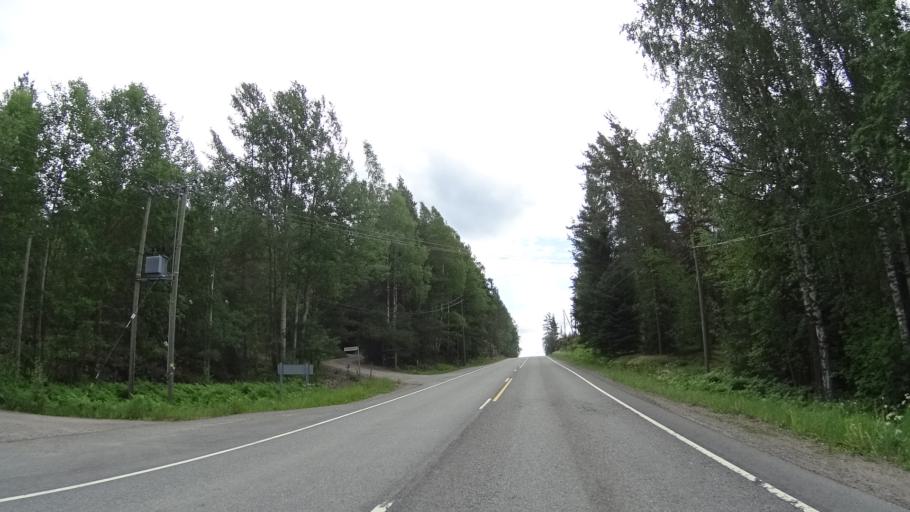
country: FI
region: Uusimaa
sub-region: Helsinki
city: Vihti
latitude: 60.2953
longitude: 24.3898
